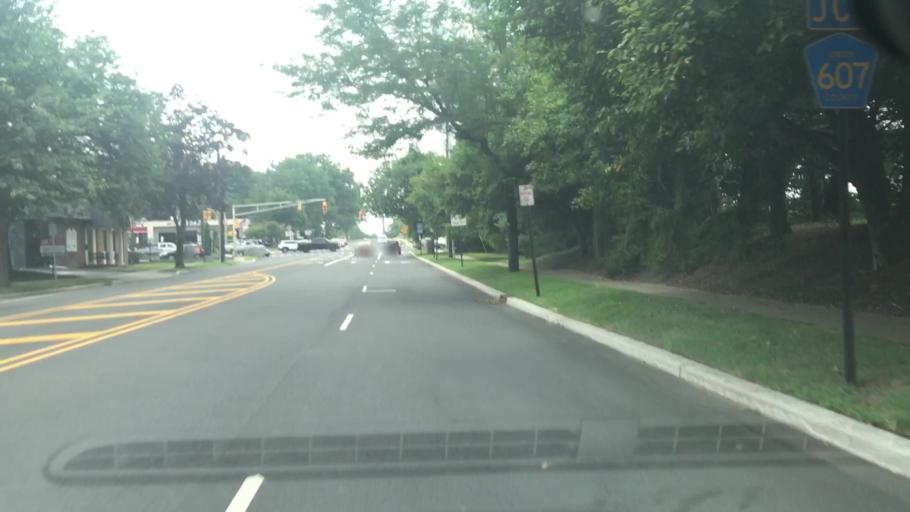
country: US
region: New Jersey
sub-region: Union County
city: Clark
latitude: 40.6353
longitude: -74.3040
